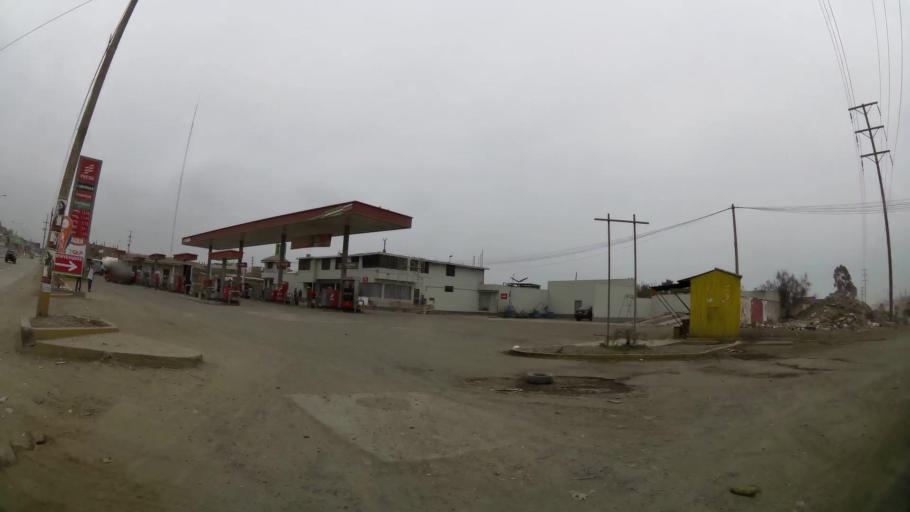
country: PE
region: Lima
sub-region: Lima
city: Surco
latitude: -12.1932
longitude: -76.9648
